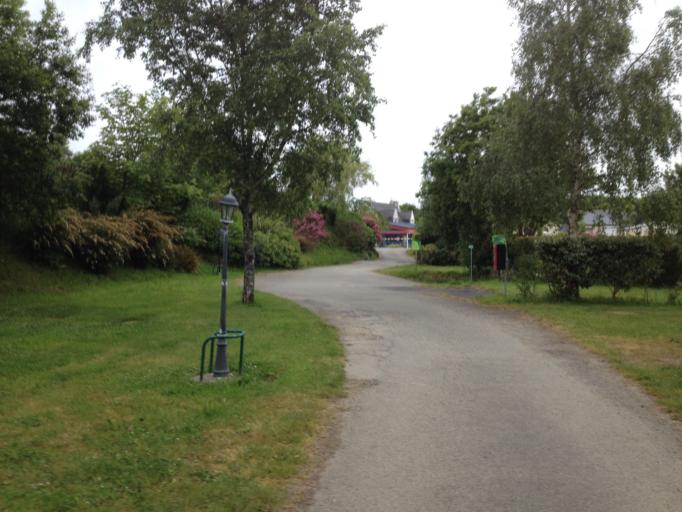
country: FR
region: Brittany
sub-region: Departement du Finistere
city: Roscanvel
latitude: 48.3651
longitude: -4.5389
